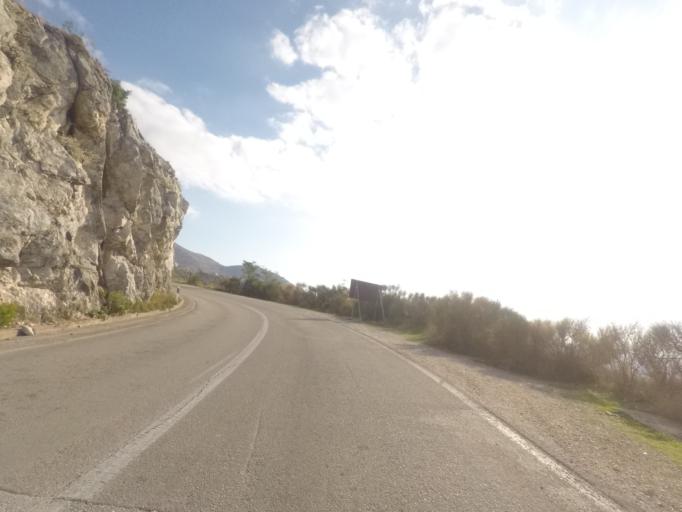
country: HR
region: Dubrovacko-Neretvanska
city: Cibaca
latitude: 42.6568
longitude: 18.1620
